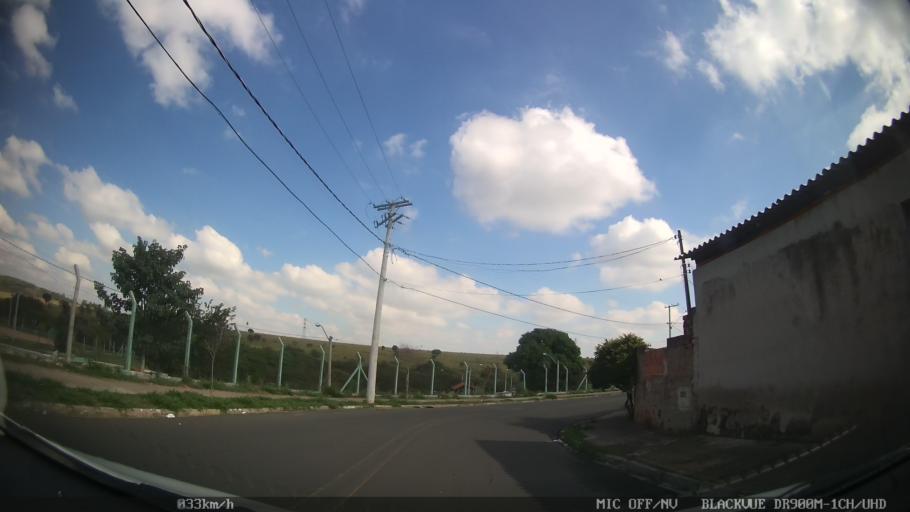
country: BR
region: Sao Paulo
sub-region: Indaiatuba
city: Indaiatuba
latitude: -22.9762
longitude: -47.1803
